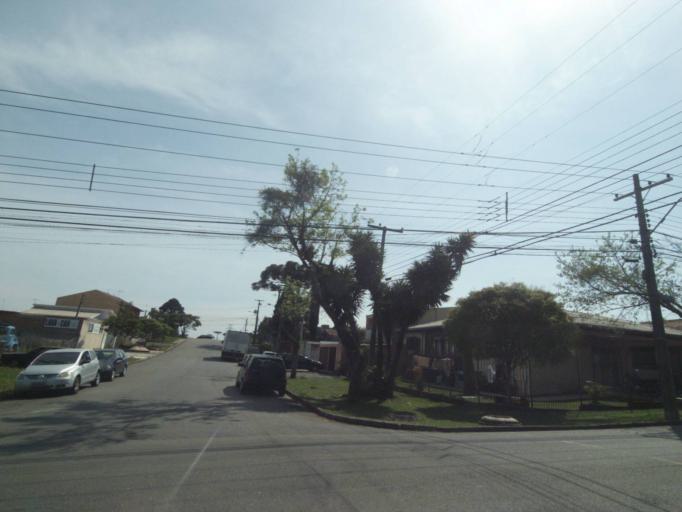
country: BR
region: Parana
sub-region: Curitiba
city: Curitiba
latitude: -25.4658
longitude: -49.3107
